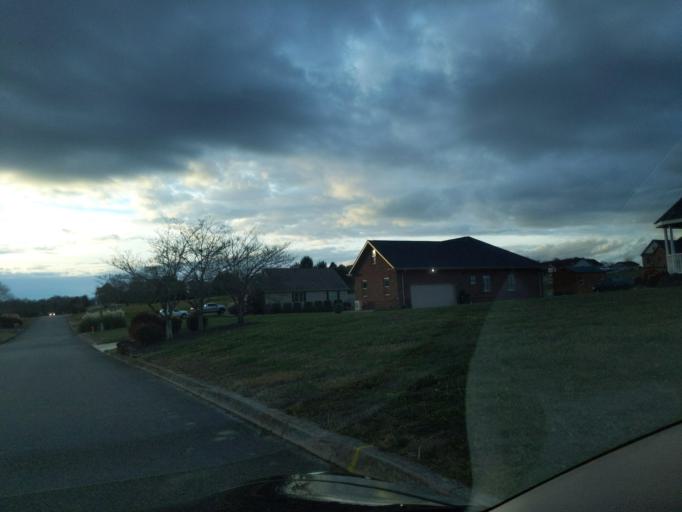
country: US
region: Tennessee
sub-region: Jefferson County
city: Dandridge
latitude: 35.9857
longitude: -83.4644
